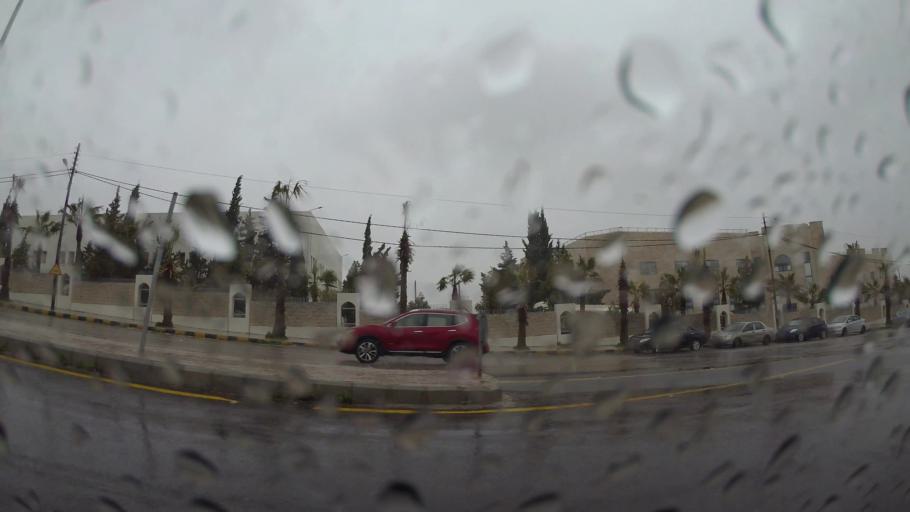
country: JO
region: Amman
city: Al Jubayhah
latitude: 32.0152
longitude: 35.8929
